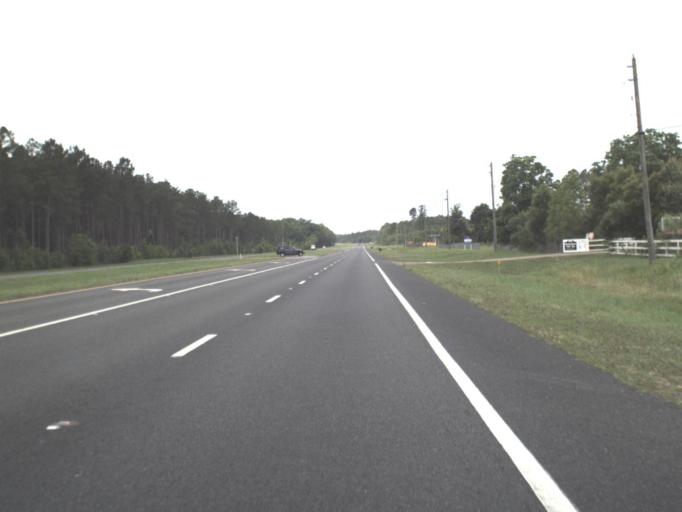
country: US
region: Florida
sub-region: Nassau County
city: Yulee
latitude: 30.6149
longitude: -81.7209
